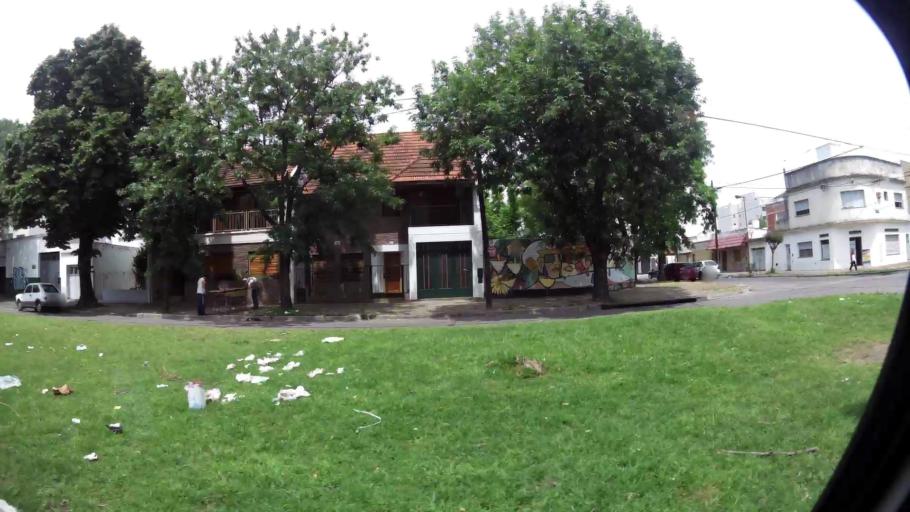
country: AR
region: Buenos Aires
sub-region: Partido de La Plata
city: La Plata
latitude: -34.9446
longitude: -57.9552
